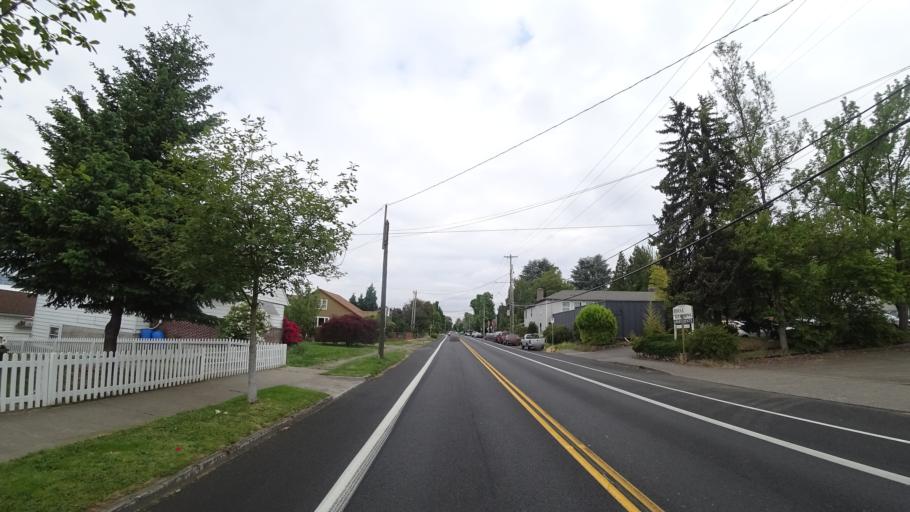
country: US
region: Oregon
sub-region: Clackamas County
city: Milwaukie
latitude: 45.4853
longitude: -122.6375
